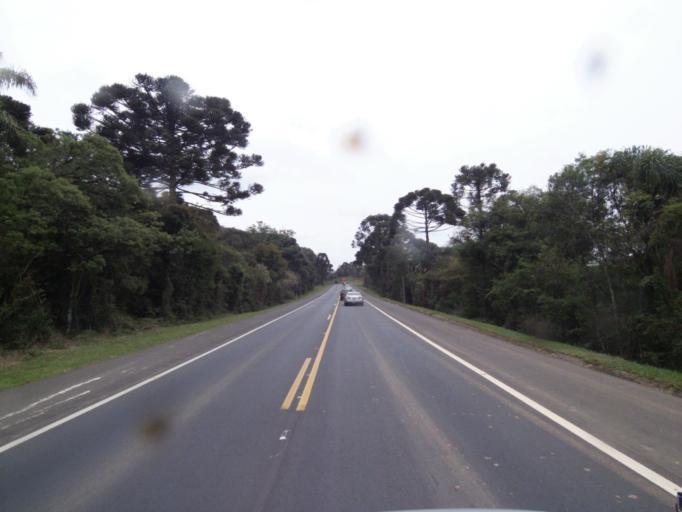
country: BR
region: Parana
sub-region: Irati
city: Irati
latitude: -25.4638
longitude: -50.5460
